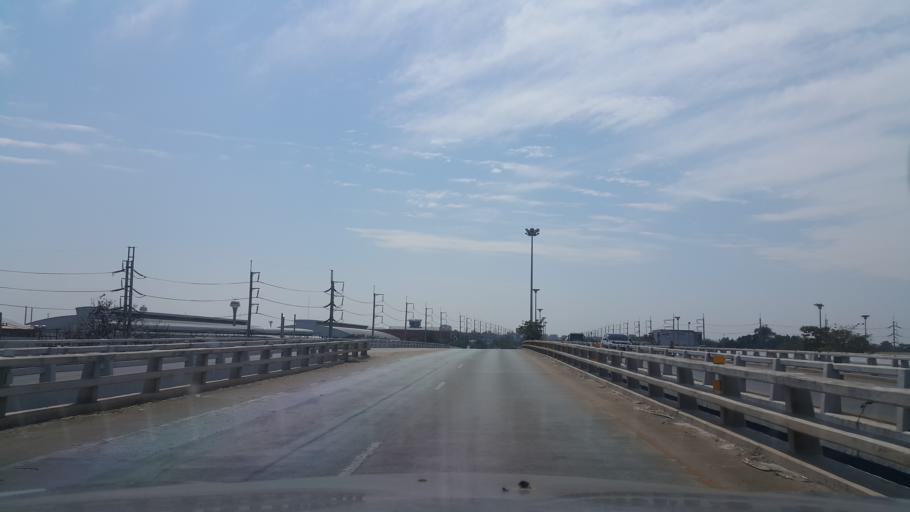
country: TH
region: Nakhon Ratchasima
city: Nakhon Ratchasima
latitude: 14.9598
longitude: 102.0535
